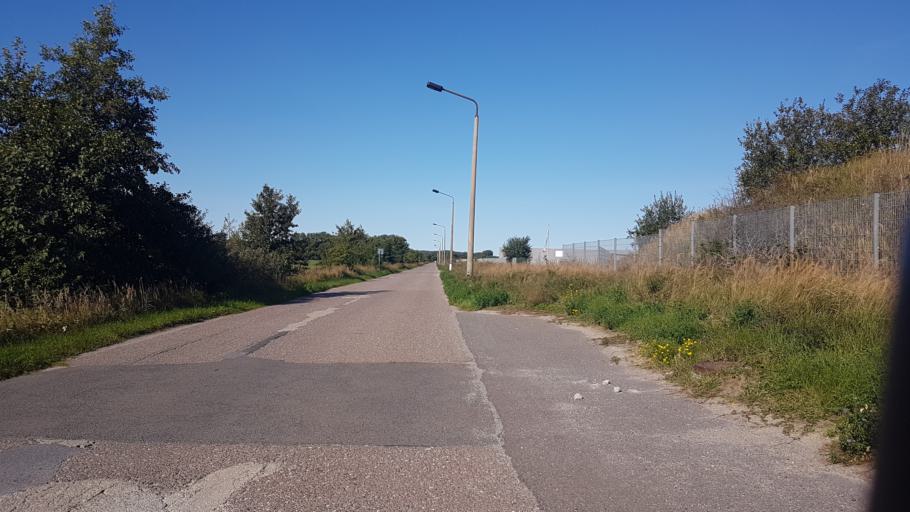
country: DE
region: Mecklenburg-Vorpommern
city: Sagard
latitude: 54.4928
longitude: 13.5645
